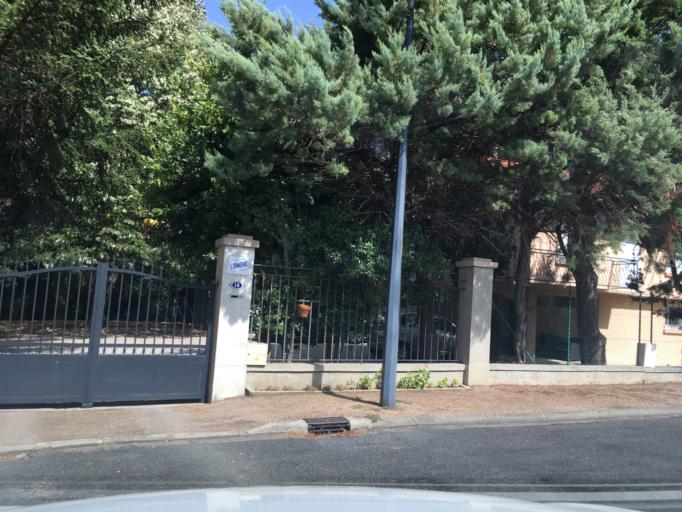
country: FR
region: Midi-Pyrenees
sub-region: Departement du Tarn
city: Castres
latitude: 43.5949
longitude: 2.2648
